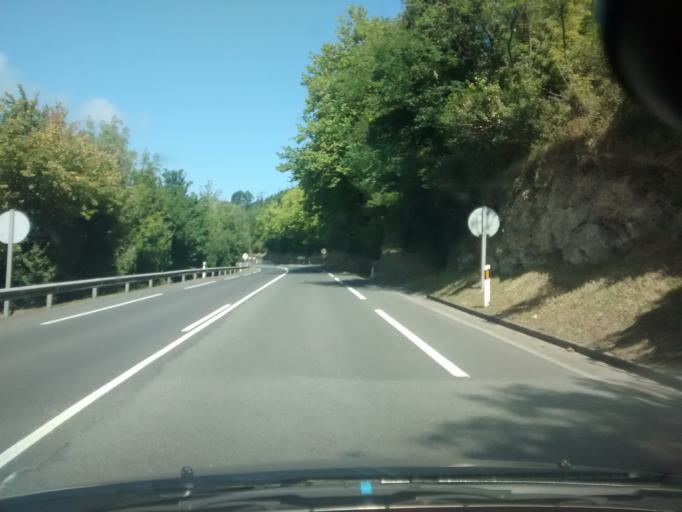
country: ES
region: Basque Country
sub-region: Provincia de Guipuzcoa
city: Zumaia
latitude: 43.2744
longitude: -2.2682
